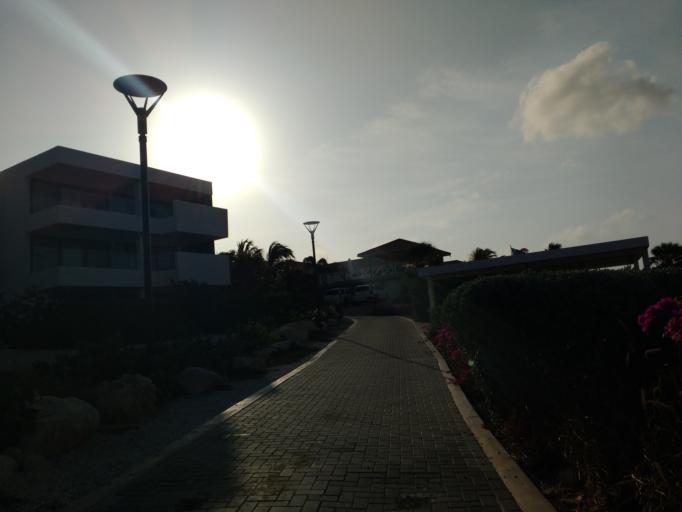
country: CW
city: Willemstad
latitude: 12.0739
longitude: -68.8780
